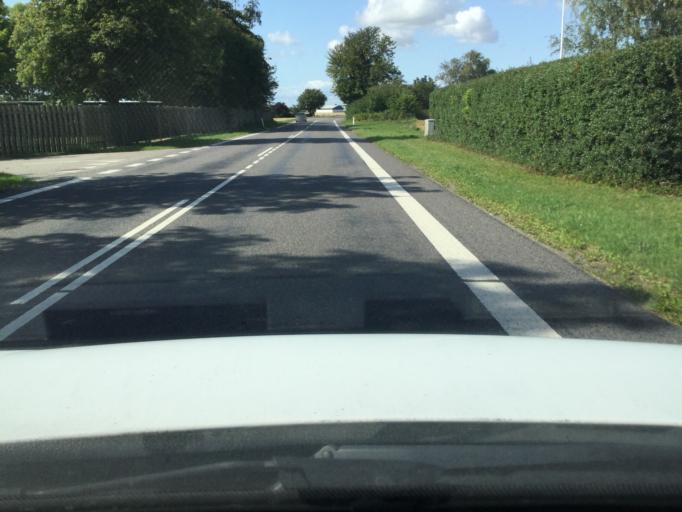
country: DK
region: Zealand
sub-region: Lolland Kommune
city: Rodby
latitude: 54.7918
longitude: 11.2803
